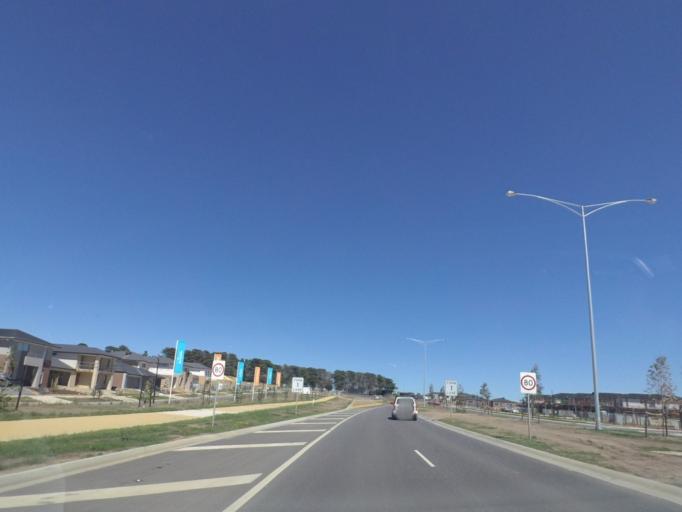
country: AU
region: Victoria
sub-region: Hume
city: Craigieburn
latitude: -37.5351
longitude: 144.8980
